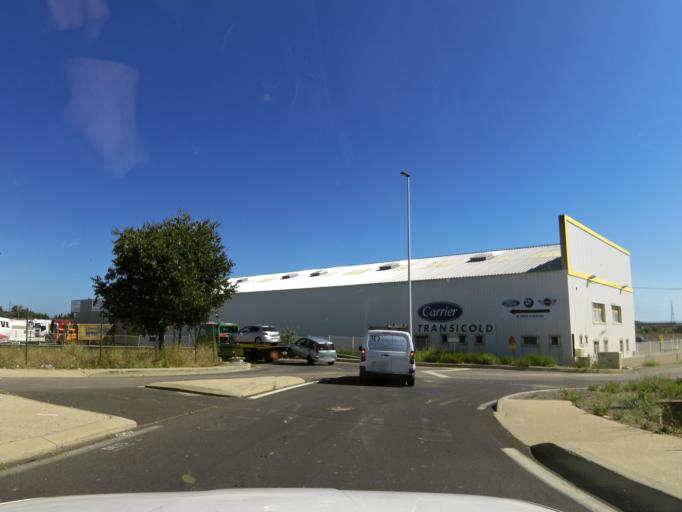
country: FR
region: Languedoc-Roussillon
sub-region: Departement de l'Herault
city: Montpellier
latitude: 43.5747
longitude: 3.8675
